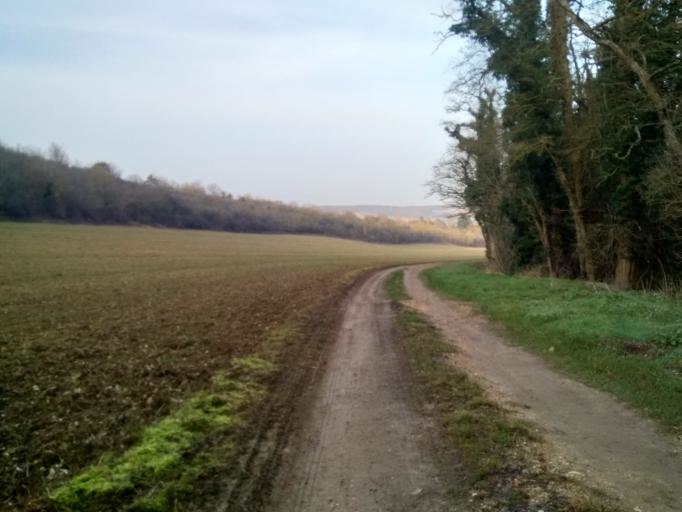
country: FR
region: Bourgogne
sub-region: Departement de l'Yonne
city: Malay-le-Grand
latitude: 48.1631
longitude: 3.3392
